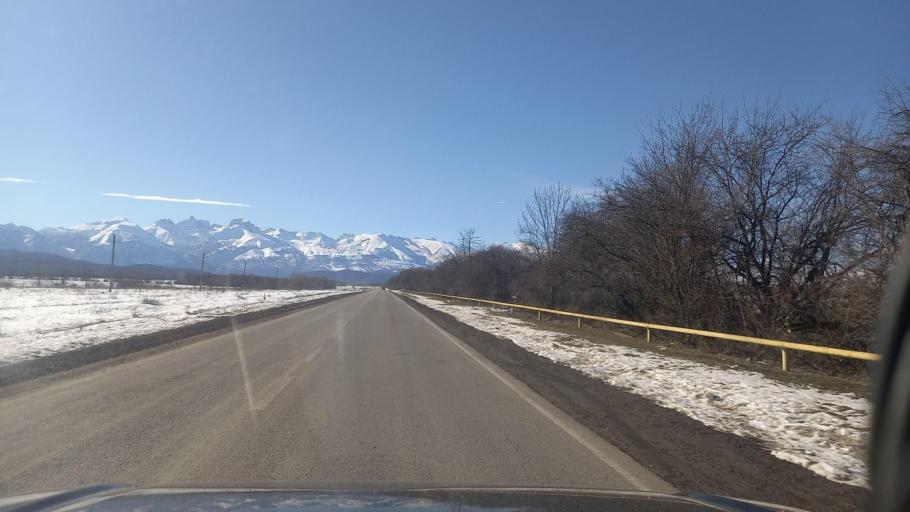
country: RU
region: North Ossetia
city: Chikola
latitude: 43.1823
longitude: 43.8920
